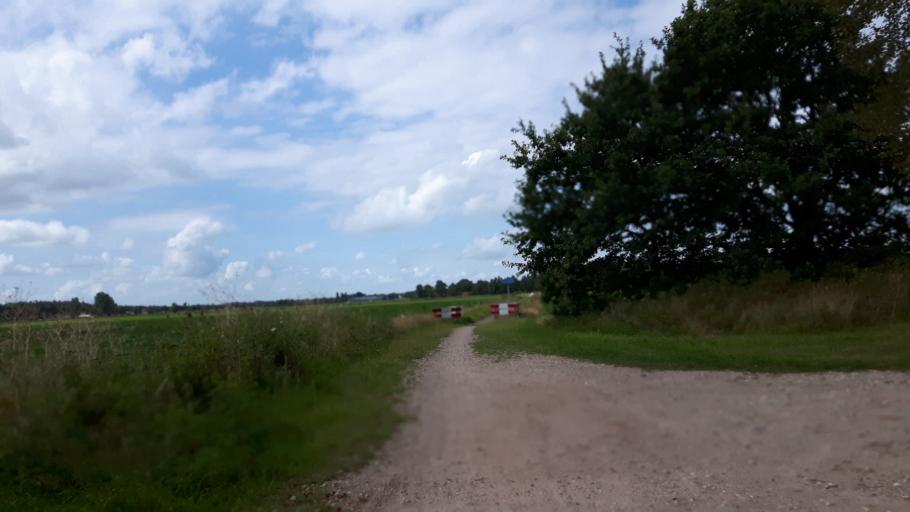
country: NL
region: Groningen
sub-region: Gemeente Leek
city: Leek
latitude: 53.0815
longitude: 6.3314
